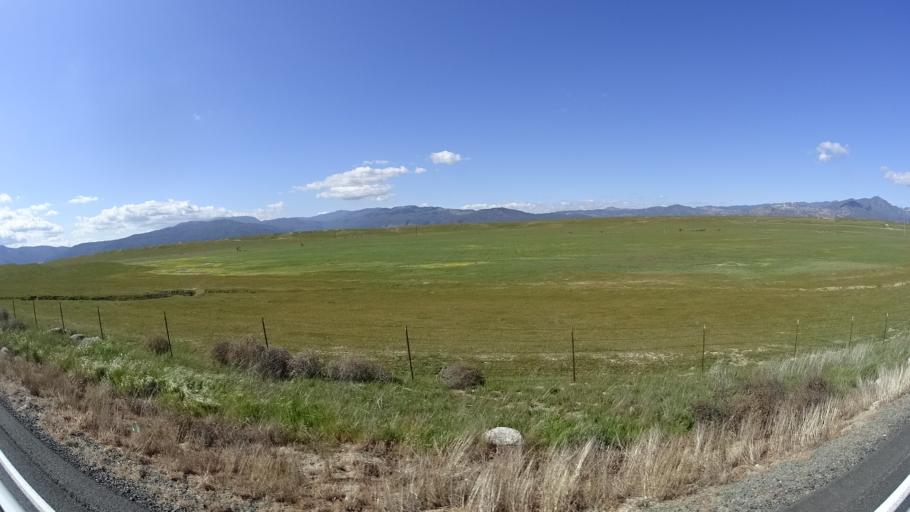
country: US
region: California
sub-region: San Diego County
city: Julian
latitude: 33.2420
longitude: -116.6871
